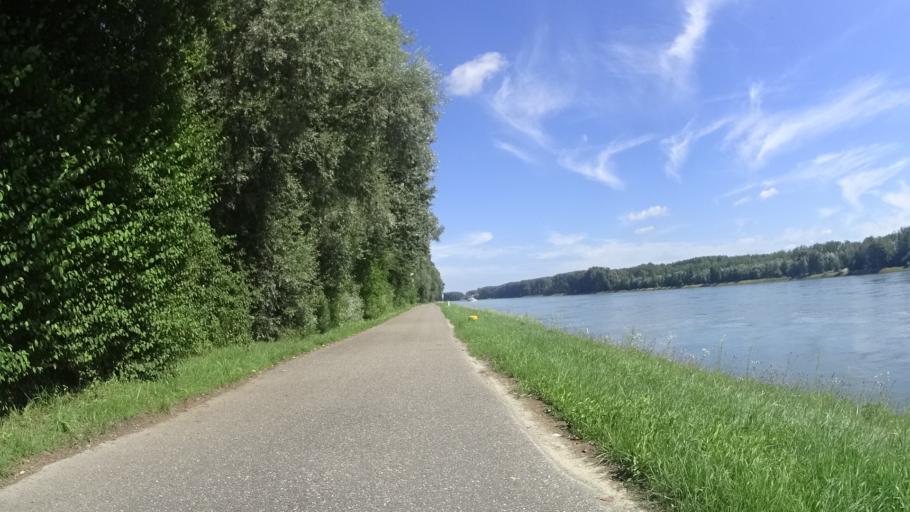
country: DE
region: Rheinland-Pfalz
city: Germersheim
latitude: 49.1932
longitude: 8.3818
